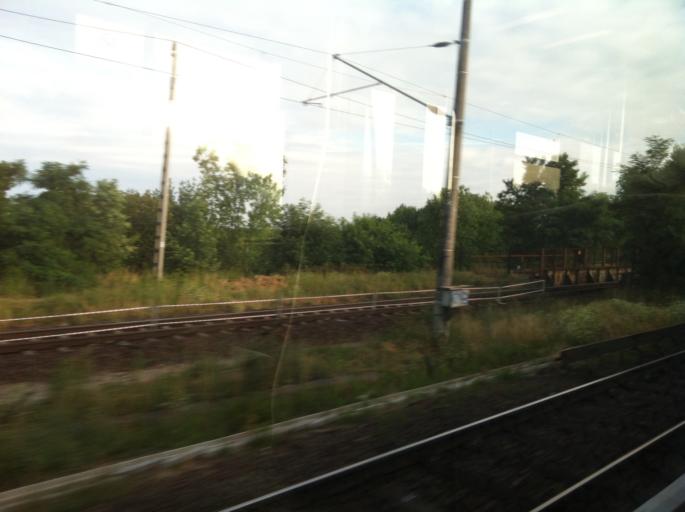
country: DE
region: Berlin
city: Blankenburg
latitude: 52.6070
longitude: 13.4603
